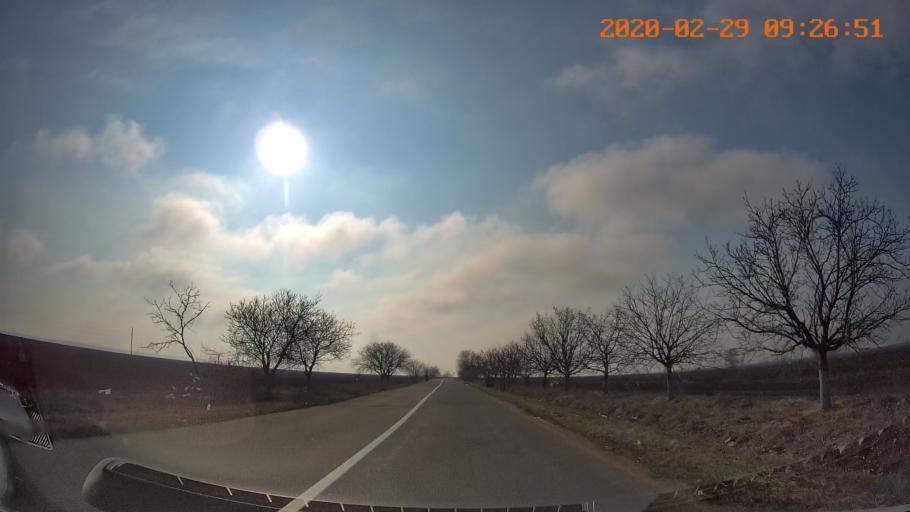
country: MD
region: Telenesti
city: Pervomaisc
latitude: 46.7016
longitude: 29.9450
